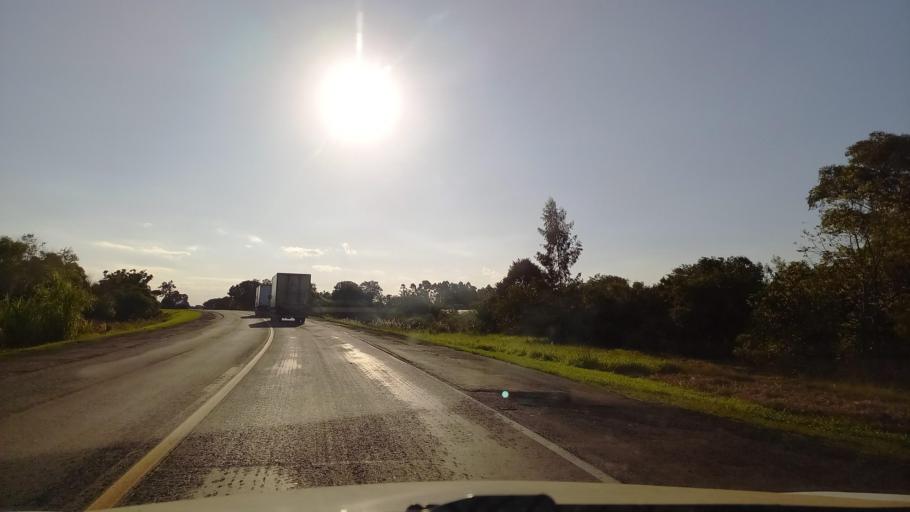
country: BR
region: Rio Grande do Sul
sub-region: Venancio Aires
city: Venancio Aires
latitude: -29.6691
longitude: -52.0266
